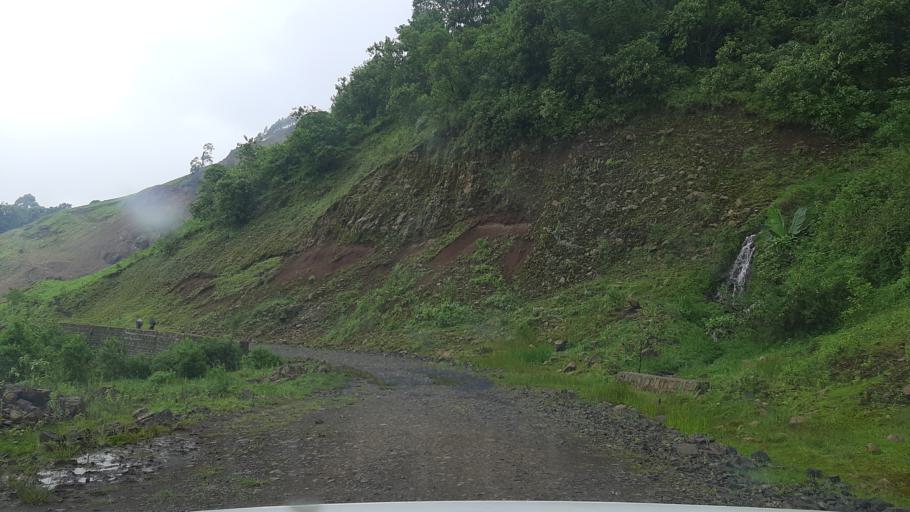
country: ET
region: Southern Nations, Nationalities, and People's Region
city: Bonga
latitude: 7.1420
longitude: 36.5686
